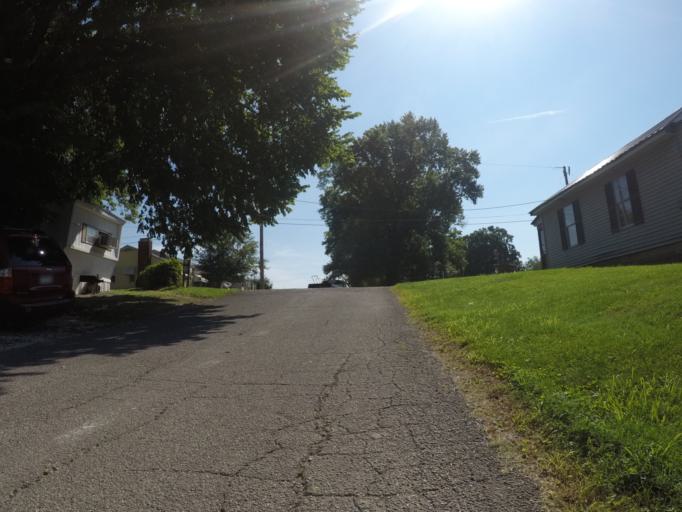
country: US
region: West Virginia
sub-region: Cabell County
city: Huntington
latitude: 38.4055
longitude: -82.4842
